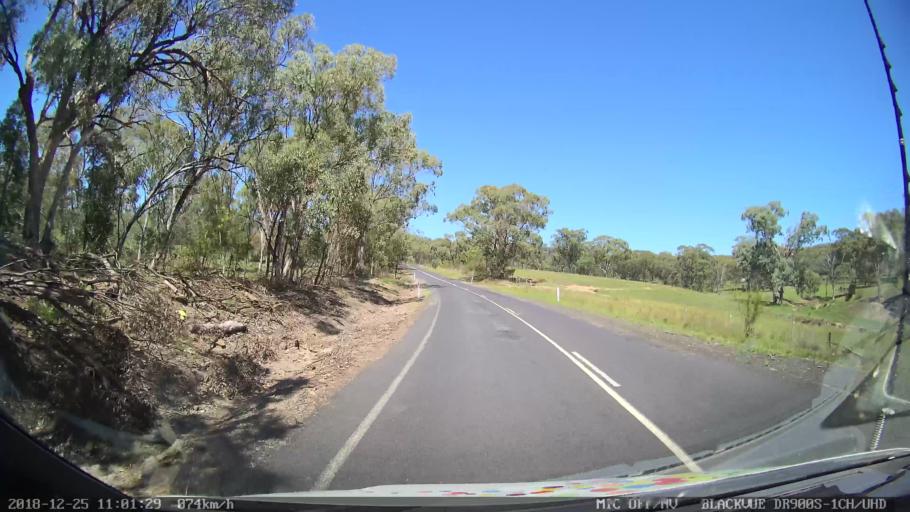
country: AU
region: New South Wales
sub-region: Upper Hunter Shire
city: Merriwa
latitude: -32.4049
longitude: 150.2011
